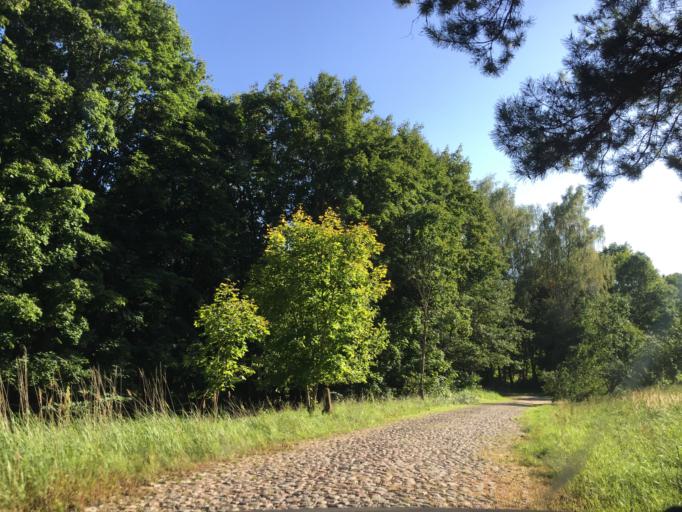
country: LT
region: Panevezys
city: Rokiskis
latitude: 55.8227
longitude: 25.8990
